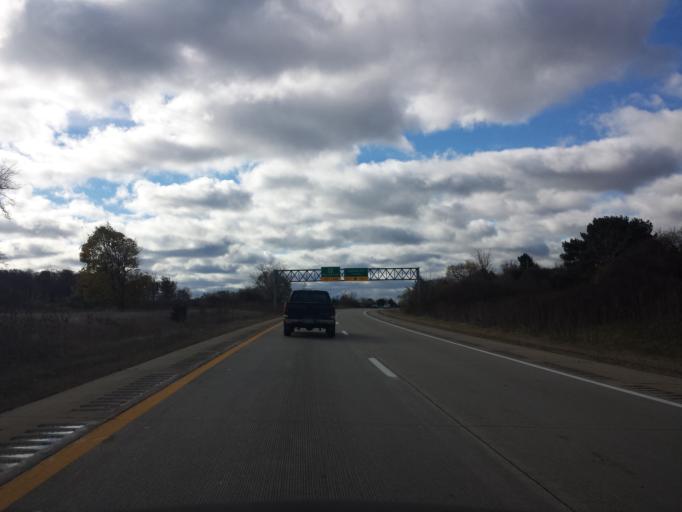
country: US
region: Michigan
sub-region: Oakland County
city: Bloomfield Hills
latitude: 42.6156
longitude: -83.2356
